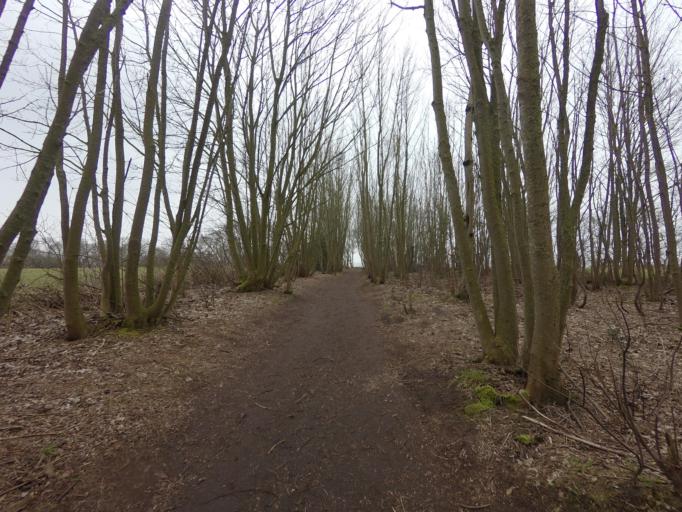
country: NL
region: Friesland
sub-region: Gemeente Gaasterlan-Sleat
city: Oudemirdum
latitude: 52.8525
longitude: 5.4778
